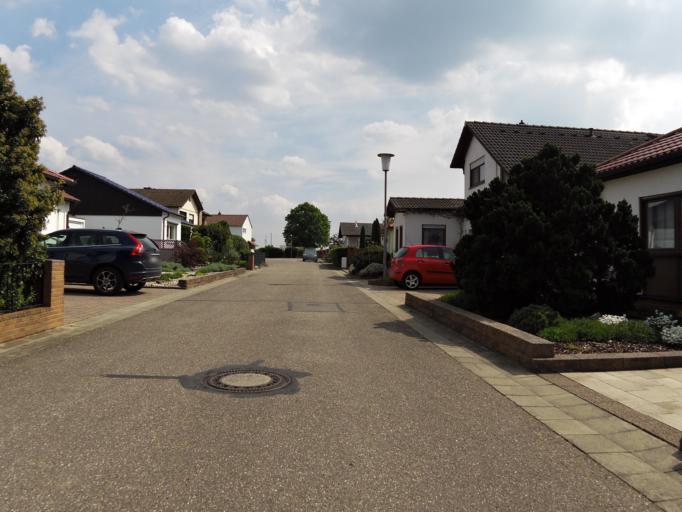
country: DE
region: Rheinland-Pfalz
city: Meckenheim
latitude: 49.4036
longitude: 8.2469
